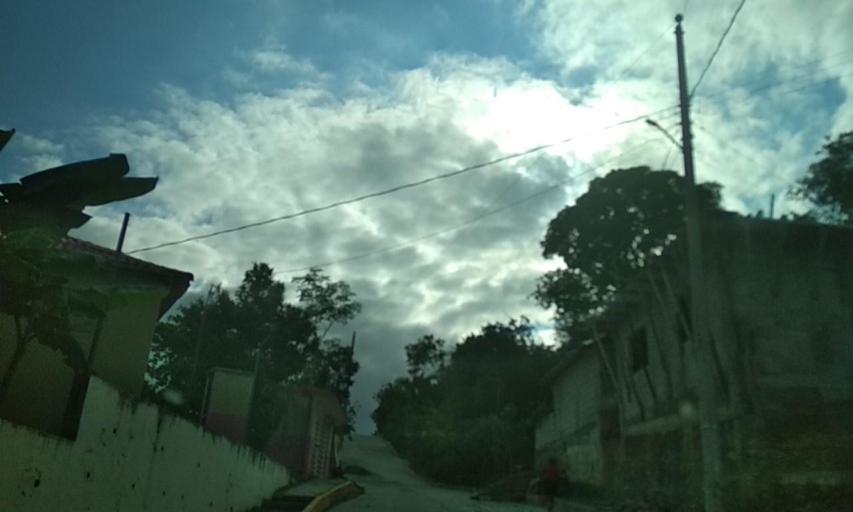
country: MX
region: Veracruz
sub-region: Papantla
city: Polutla
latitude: 20.5723
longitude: -97.2531
